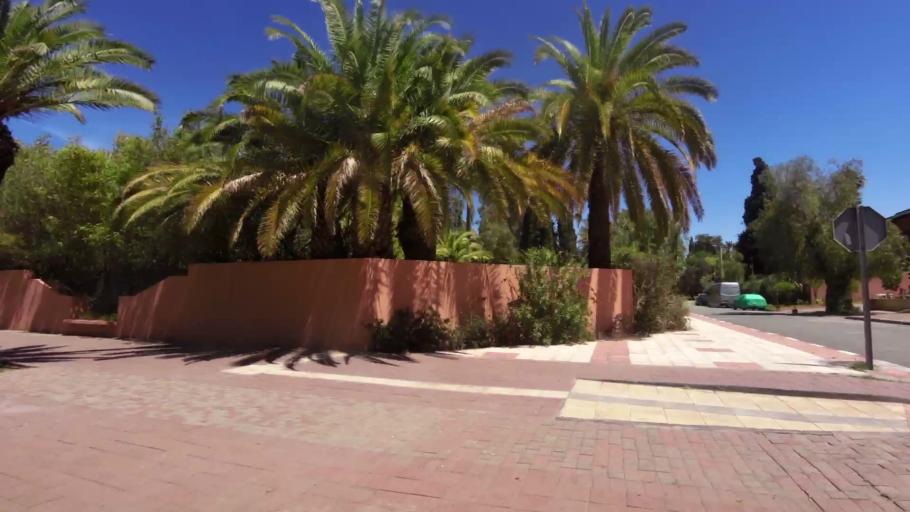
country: MA
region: Marrakech-Tensift-Al Haouz
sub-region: Marrakech
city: Marrakesh
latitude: 31.6237
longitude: -8.0116
